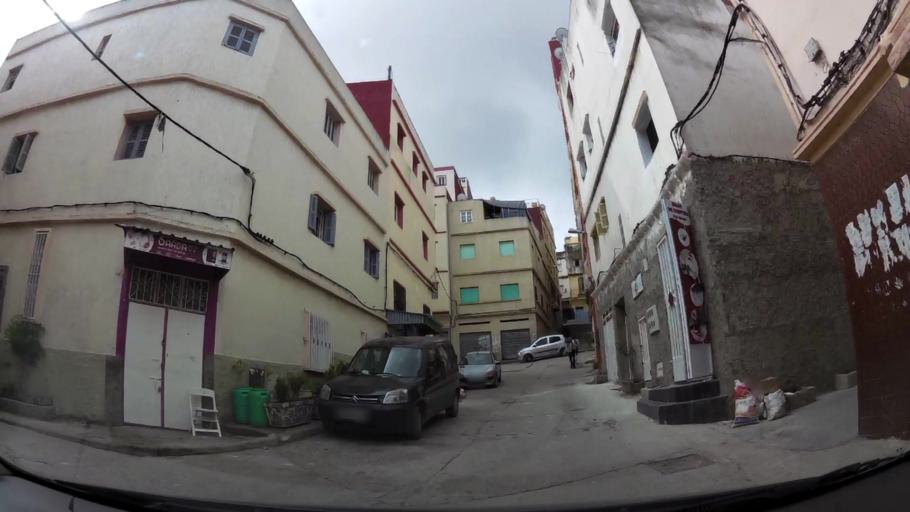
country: MA
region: Tanger-Tetouan
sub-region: Tanger-Assilah
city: Tangier
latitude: 35.7695
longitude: -5.8225
